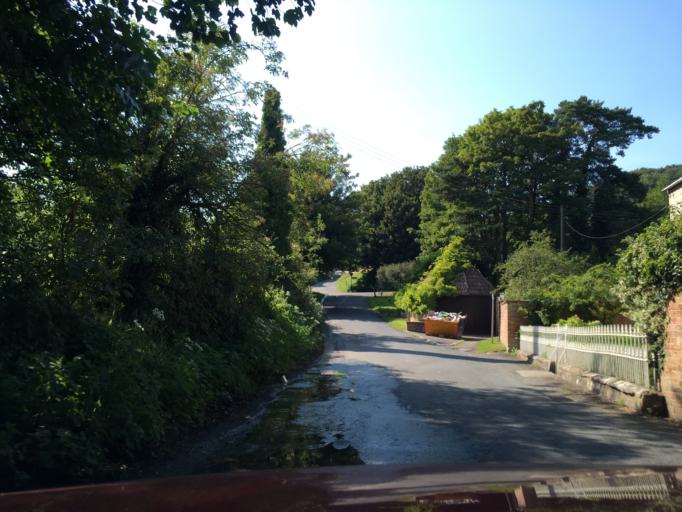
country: GB
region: England
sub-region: Gloucestershire
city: Dursley
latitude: 51.6795
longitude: -2.3107
